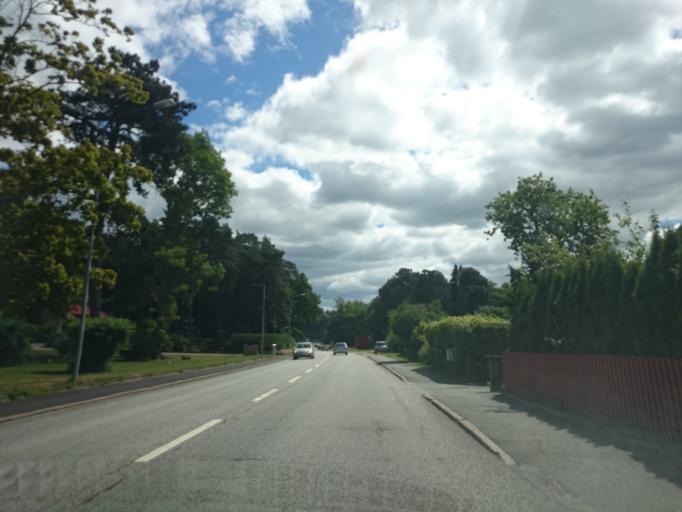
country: SE
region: Skane
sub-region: Kristianstads Kommun
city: Degeberga
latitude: 55.8285
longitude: 14.0926
